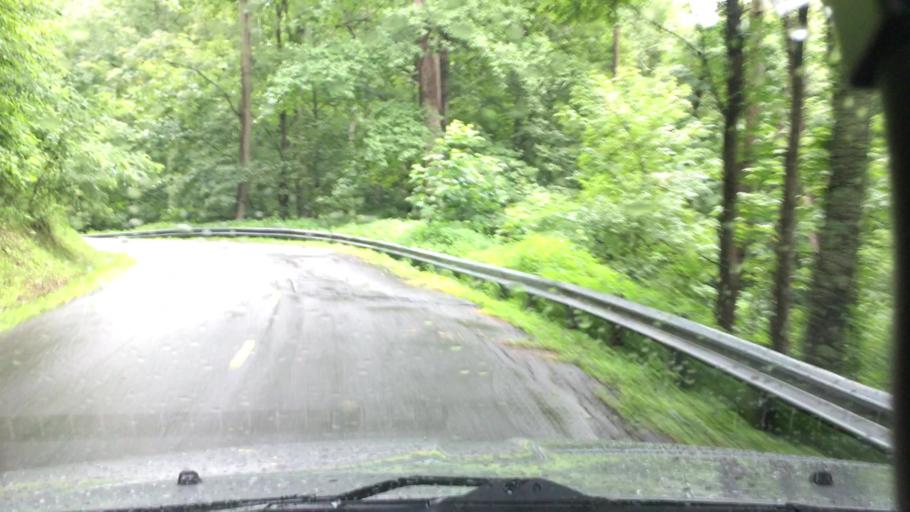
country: US
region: North Carolina
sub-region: Madison County
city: Mars Hill
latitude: 35.9448
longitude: -82.5207
